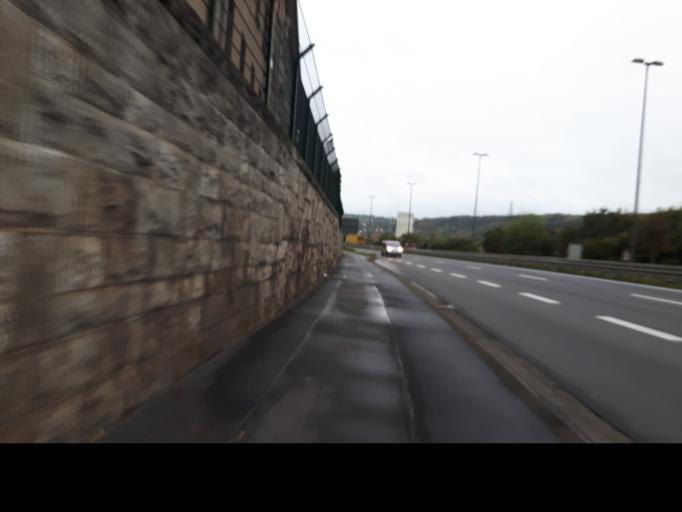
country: DE
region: Bavaria
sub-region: Regierungsbezirk Unterfranken
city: Zell am Main
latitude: 49.8072
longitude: 9.8849
